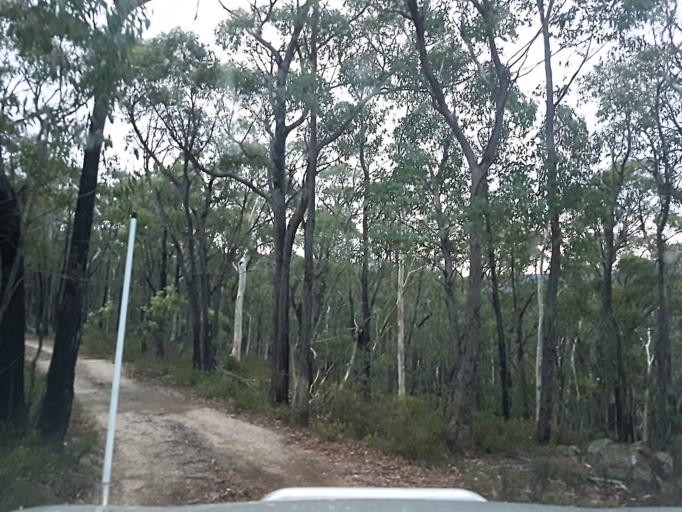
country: AU
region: New South Wales
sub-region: Snowy River
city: Jindabyne
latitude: -36.8553
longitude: 148.2305
